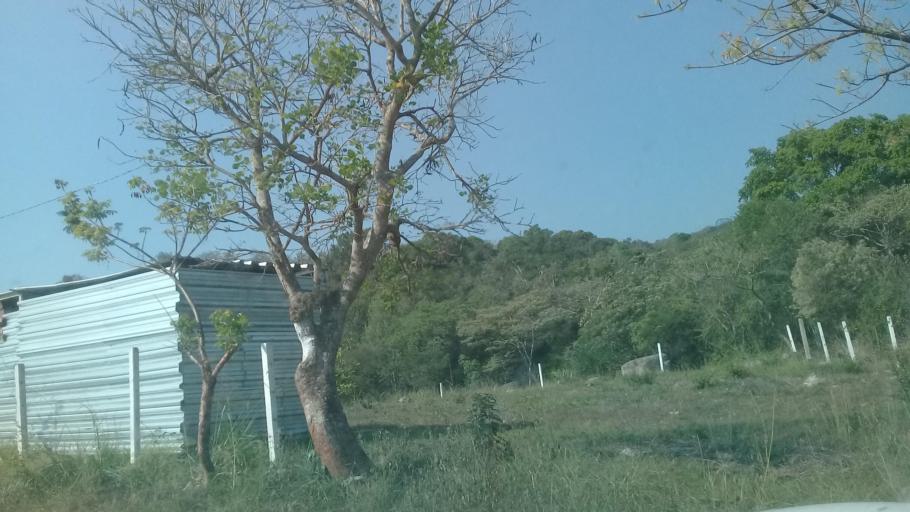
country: MX
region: Veracruz
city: El Castillo
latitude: 19.5739
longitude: -96.8373
